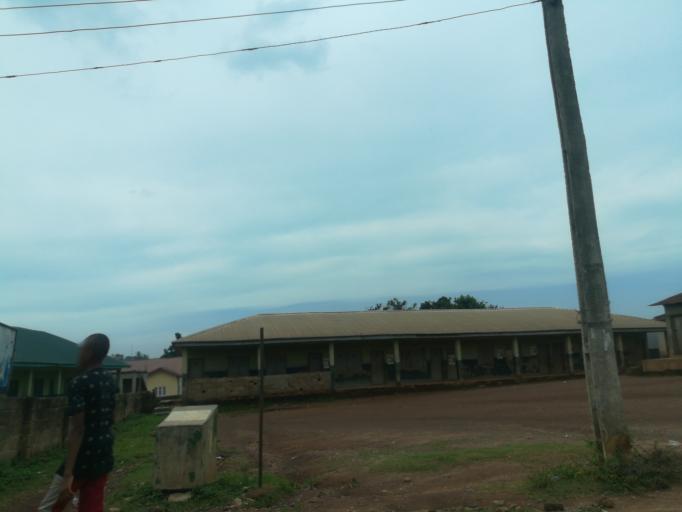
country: NG
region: Oyo
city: Ibadan
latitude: 7.3829
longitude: 3.9642
